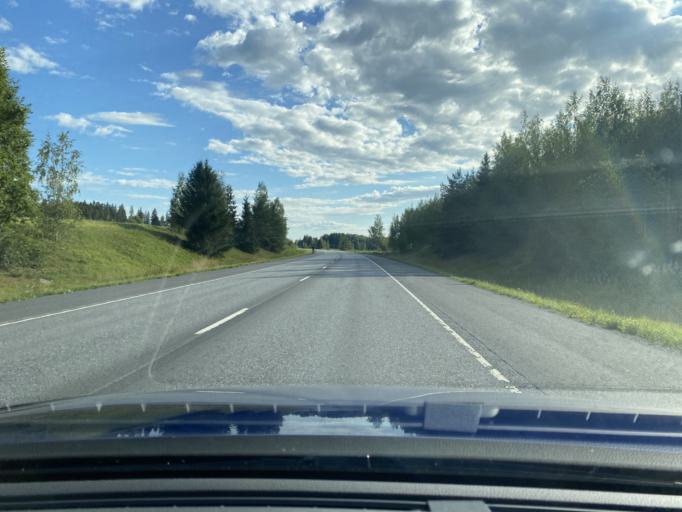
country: FI
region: Pirkanmaa
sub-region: Tampere
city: Lempaeaelae
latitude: 61.3340
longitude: 23.7793
